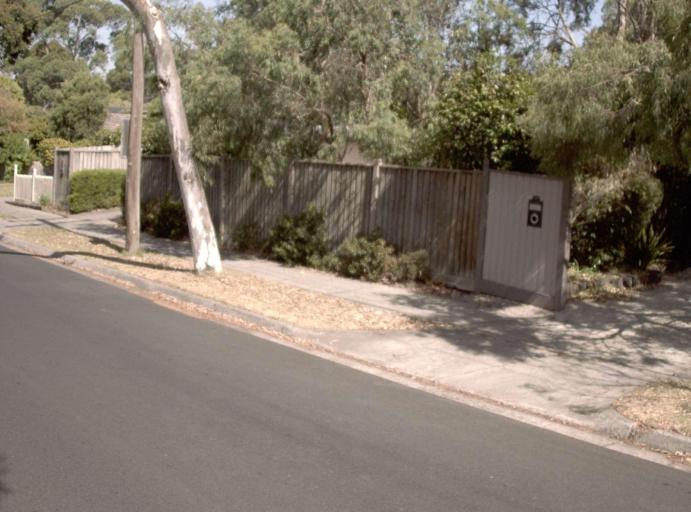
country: AU
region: Victoria
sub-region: Monash
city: Mulgrave
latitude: -37.8918
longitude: 145.1904
